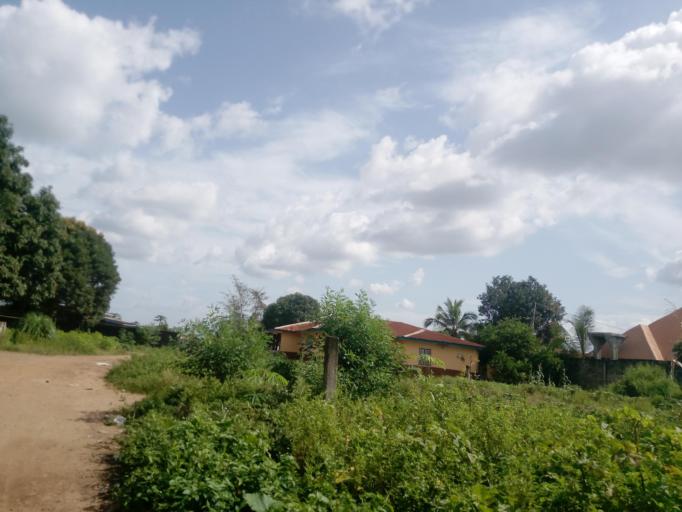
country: SL
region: Northern Province
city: Makeni
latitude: 8.9034
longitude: -12.0313
